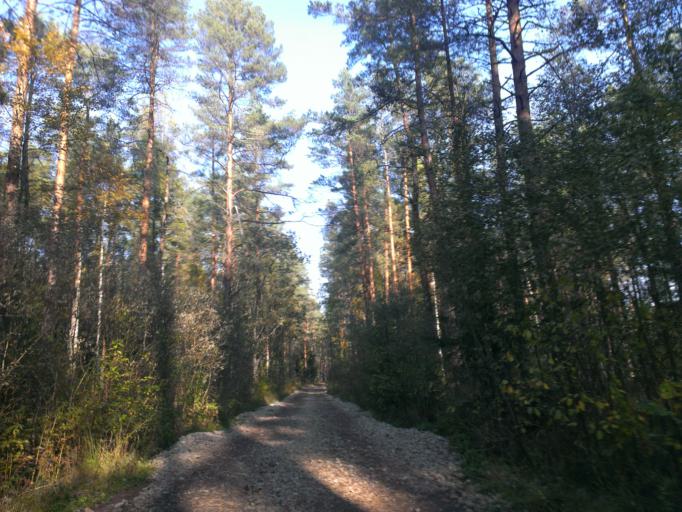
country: LV
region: Garkalne
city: Garkalne
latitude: 57.0153
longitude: 24.4645
